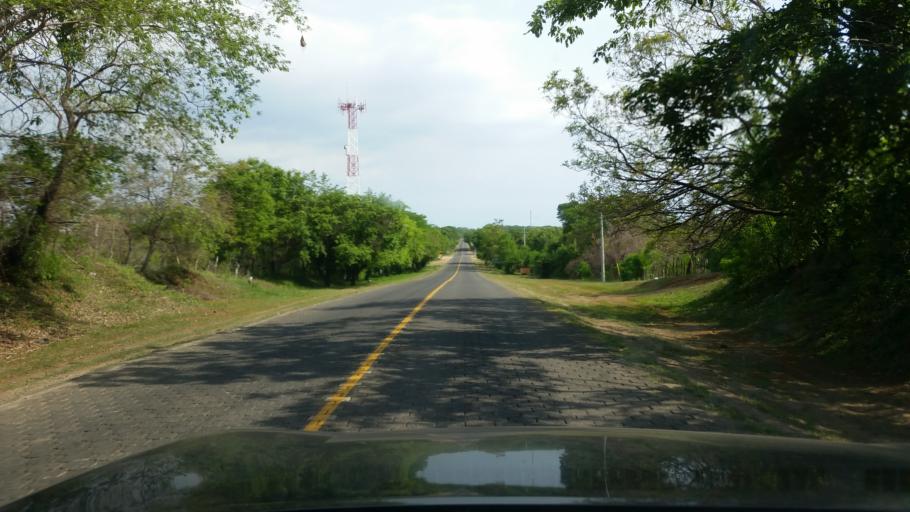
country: NI
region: Managua
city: Carlos Fonseca Amador
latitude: 11.9191
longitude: -86.5065
